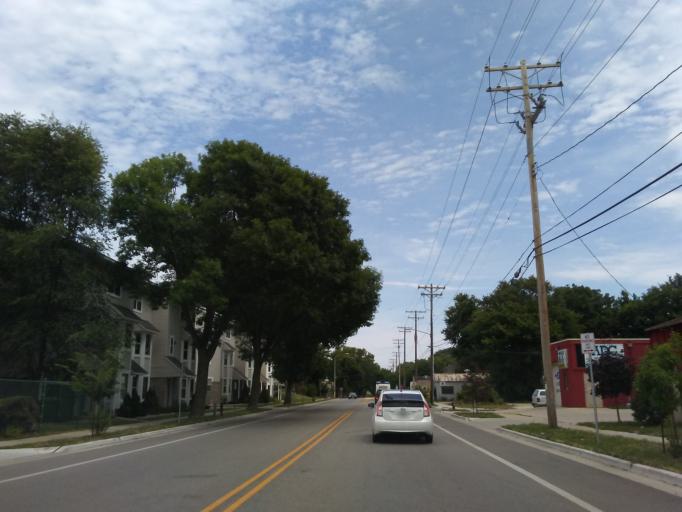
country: US
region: Wisconsin
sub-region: Dane County
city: Maple Bluff
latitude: 43.1068
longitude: -89.3533
